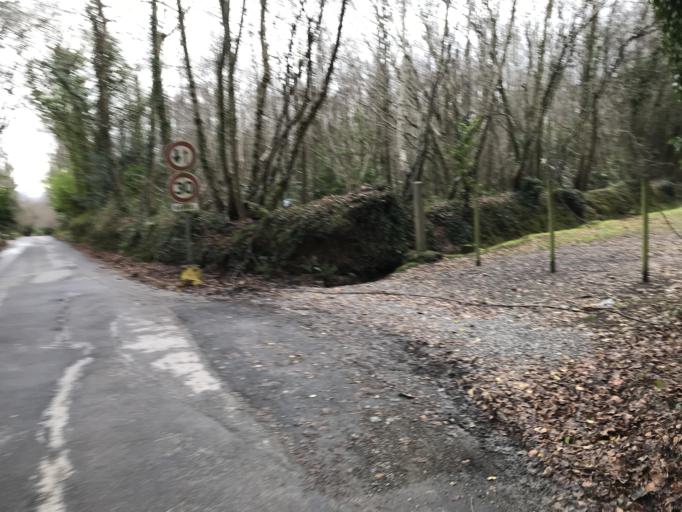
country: FR
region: Brittany
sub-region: Departement du Finistere
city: Plougastel-Daoulas
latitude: 48.3813
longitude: -4.3482
